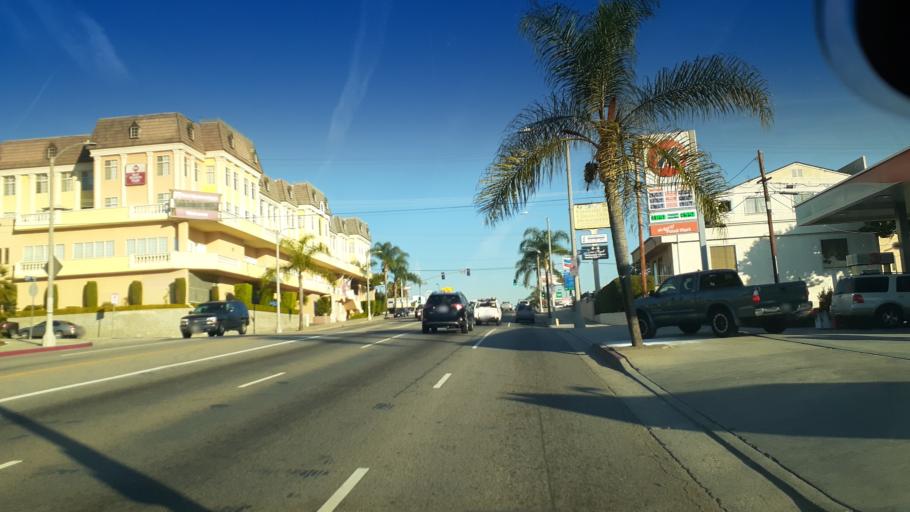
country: US
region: California
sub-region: Los Angeles County
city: San Pedro
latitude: 33.7419
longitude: -118.2922
